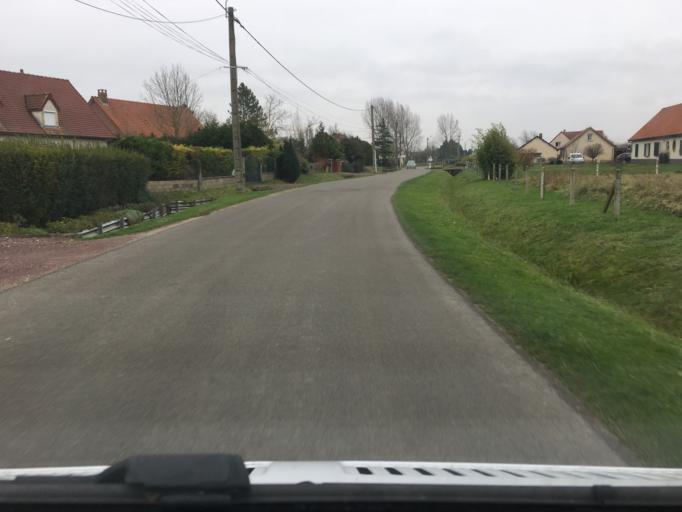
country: FR
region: Picardie
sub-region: Departement de la Somme
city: Pende
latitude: 50.1688
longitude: 1.5509
